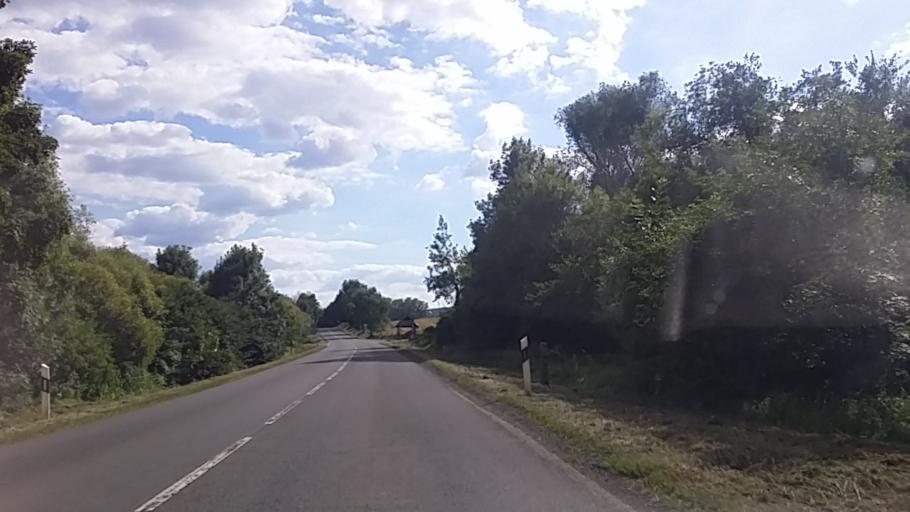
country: HU
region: Baranya
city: Sasd
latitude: 46.2798
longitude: 18.1089
